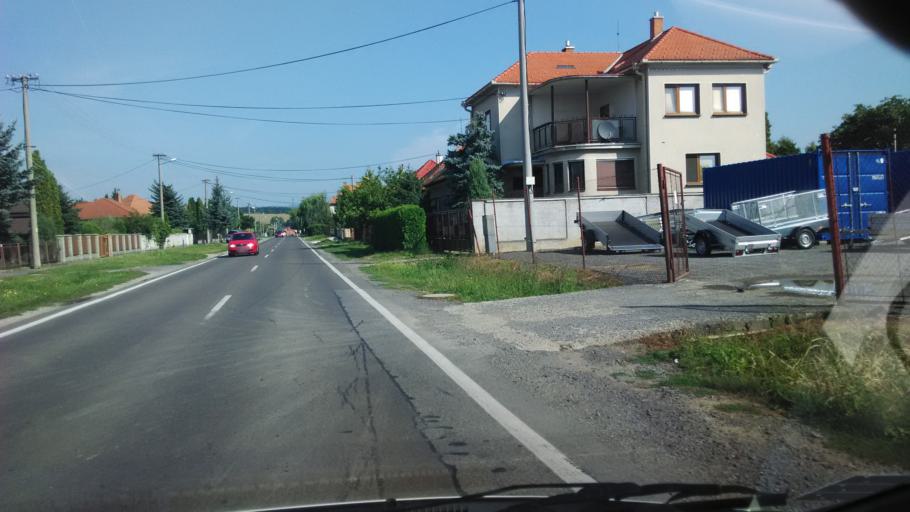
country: SK
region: Nitriansky
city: Zlate Moravce
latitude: 48.4092
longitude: 18.4100
